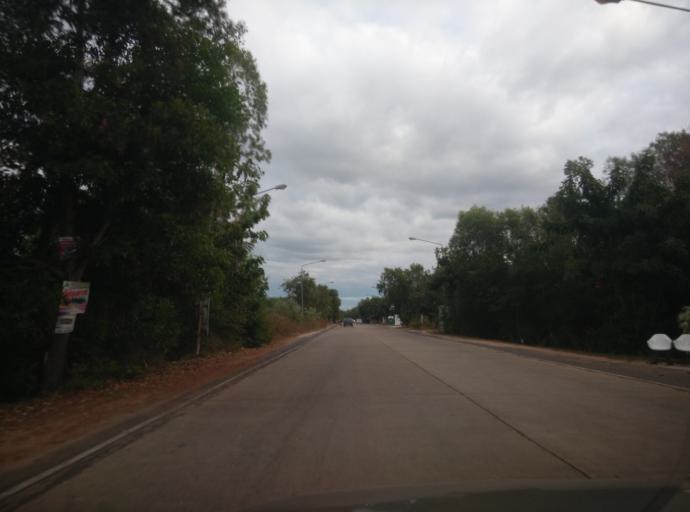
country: TH
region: Sisaket
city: Si Sa Ket
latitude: 15.1223
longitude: 104.3475
